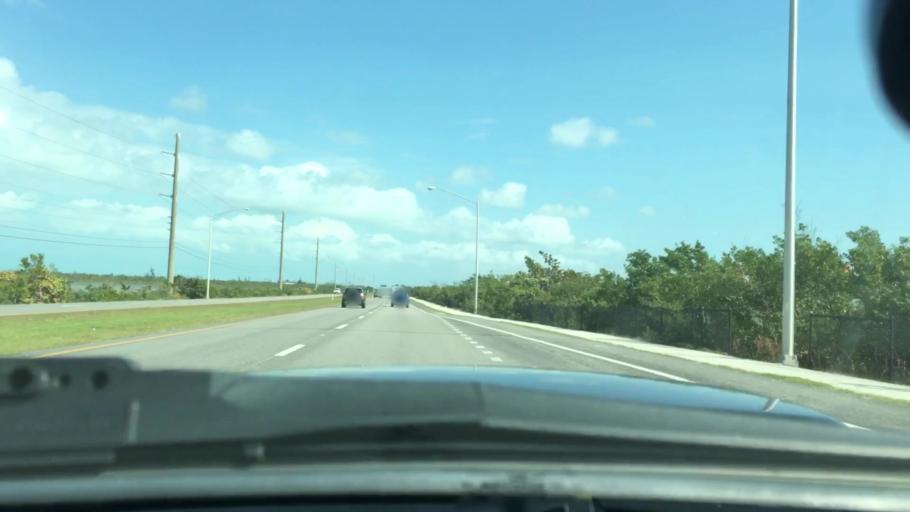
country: US
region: Florida
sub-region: Monroe County
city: Stock Island
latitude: 24.5802
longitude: -81.7063
